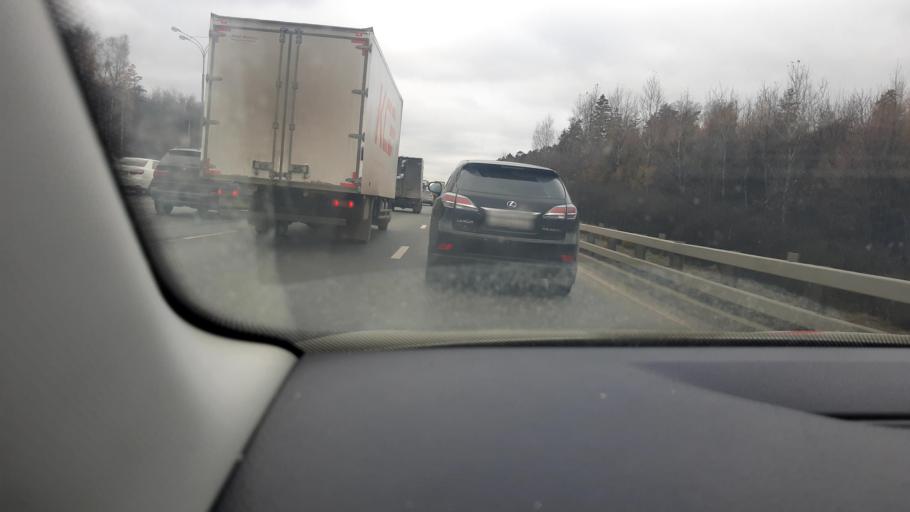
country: RU
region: Moscow
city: Chertanovo Yuzhnoye
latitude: 55.5840
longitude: 37.5619
